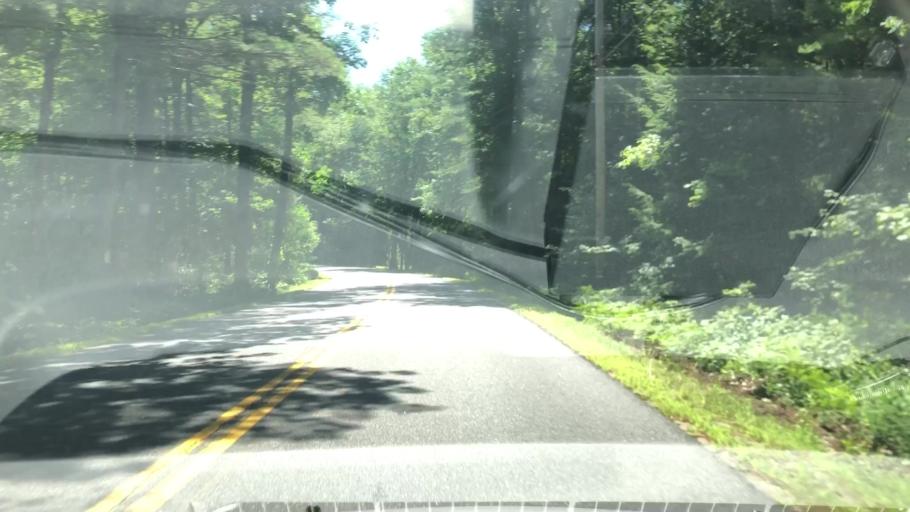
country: US
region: New Hampshire
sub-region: Hillsborough County
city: Milford
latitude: 42.8599
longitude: -71.5942
